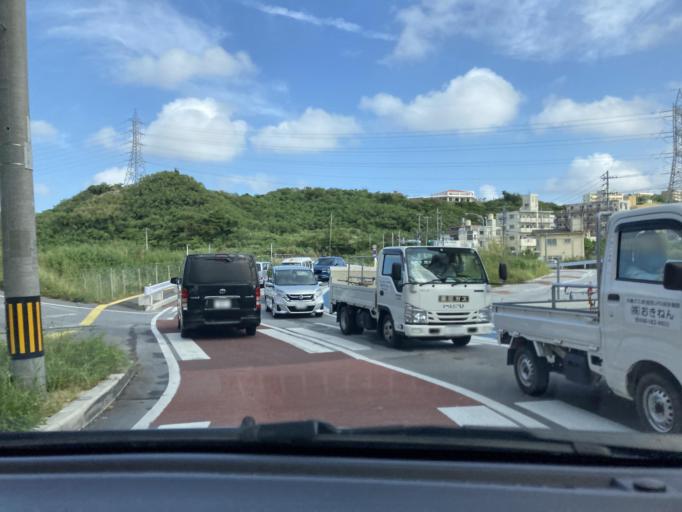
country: JP
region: Okinawa
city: Ginowan
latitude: 26.2392
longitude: 127.7491
